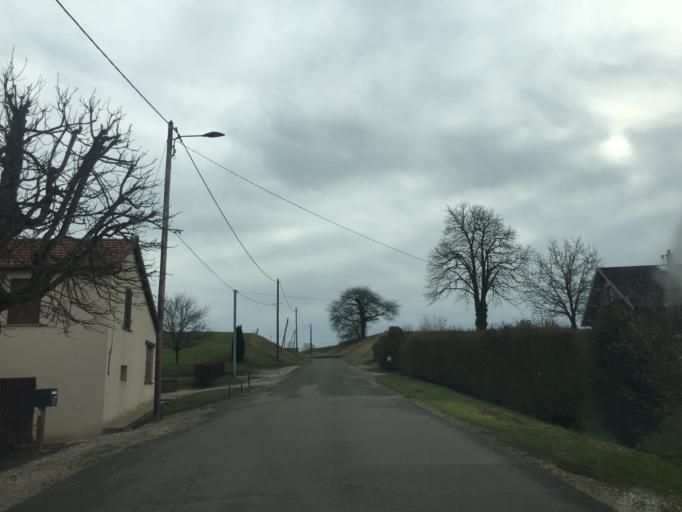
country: FR
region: Franche-Comte
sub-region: Departement du Jura
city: Chaussin
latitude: 46.9051
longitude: 5.4535
